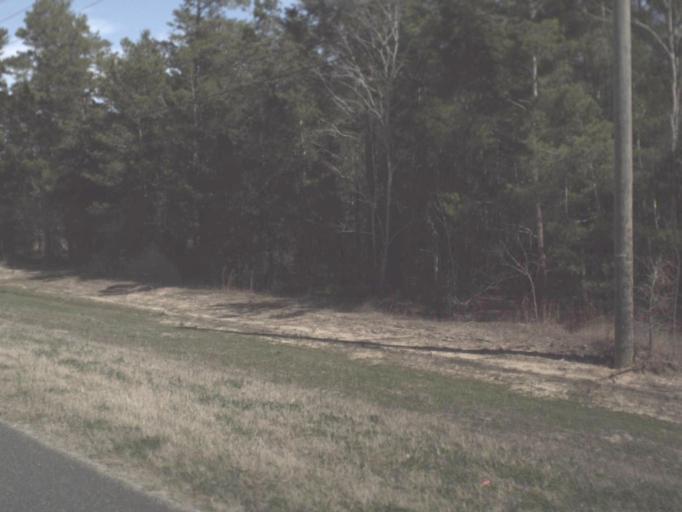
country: US
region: Florida
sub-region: Bay County
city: Lynn Haven
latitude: 30.4003
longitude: -85.6895
